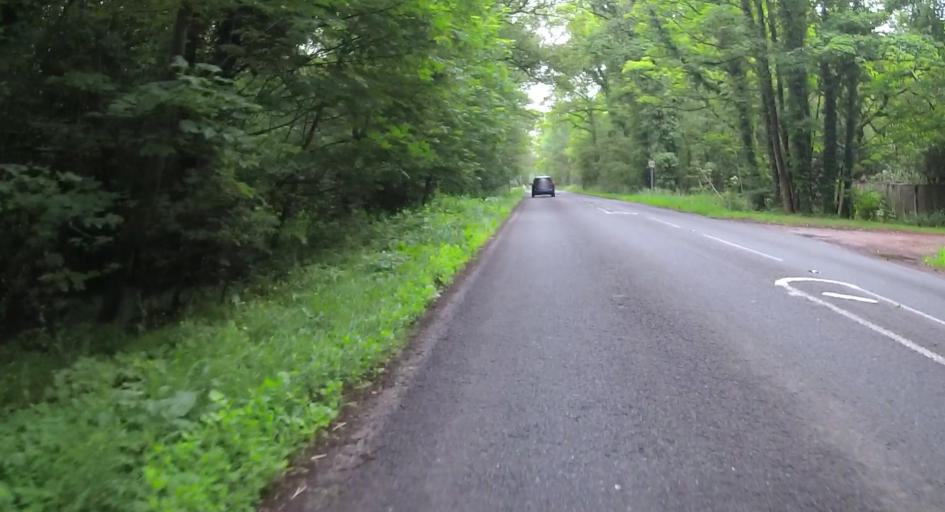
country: GB
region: England
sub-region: Hampshire
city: Hook
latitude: 51.3162
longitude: -0.9482
